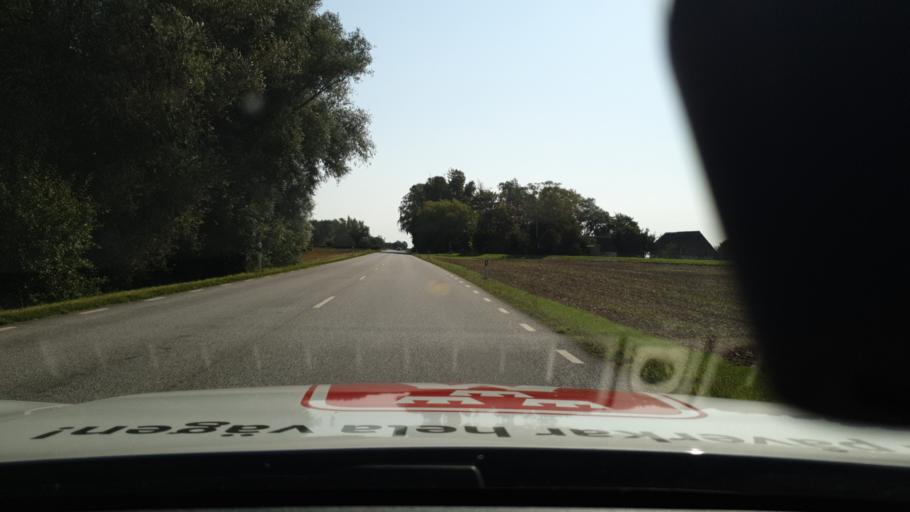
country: SE
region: Skane
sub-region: Kristianstads Kommun
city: Norra Asum
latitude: 55.9798
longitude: 14.1689
